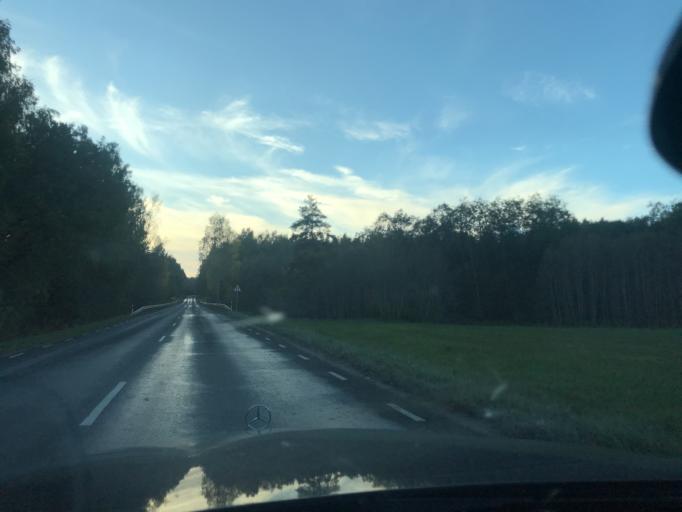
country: EE
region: Vorumaa
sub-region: Voru linn
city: Voru
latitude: 57.8784
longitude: 26.7839
